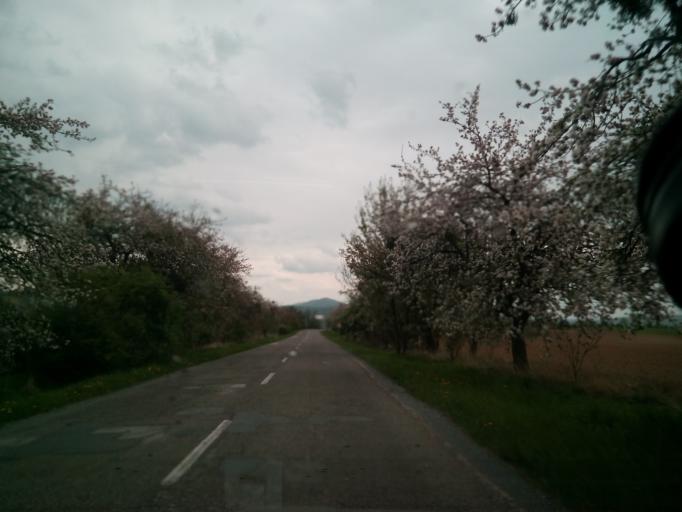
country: SK
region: Kosicky
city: Secovce
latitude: 48.7554
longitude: 21.4651
